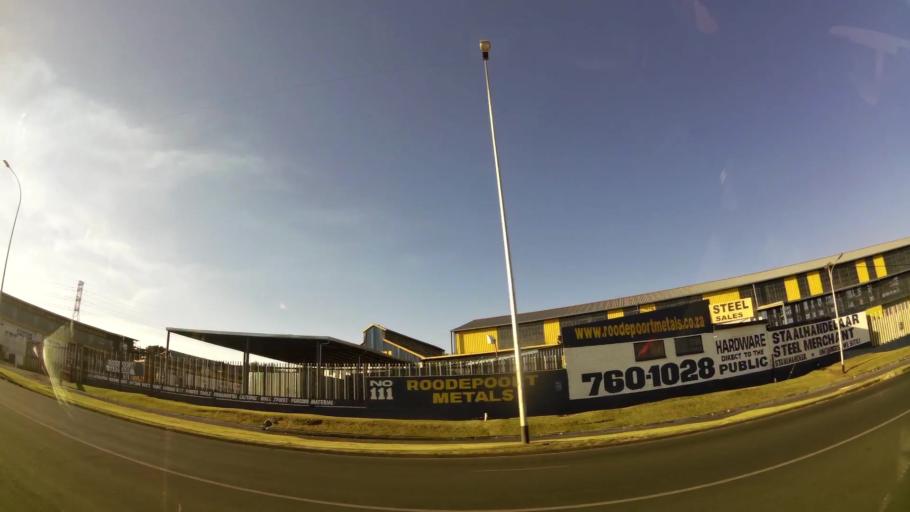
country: ZA
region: Gauteng
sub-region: City of Johannesburg Metropolitan Municipality
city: Roodepoort
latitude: -26.1434
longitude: 27.8606
